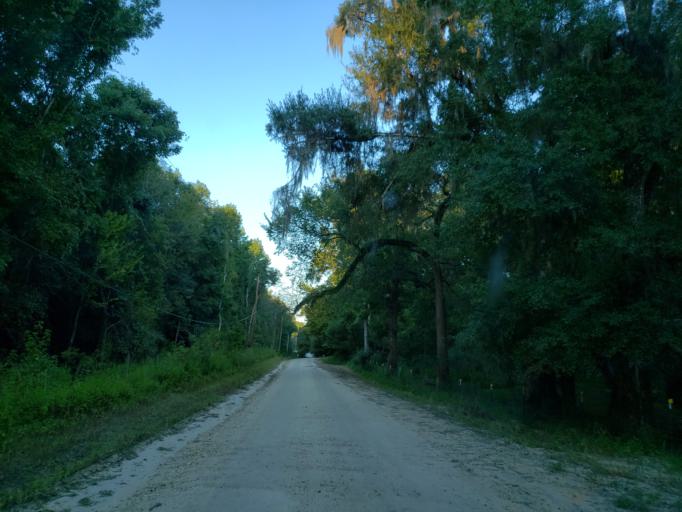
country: US
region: Florida
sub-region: Marion County
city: Citra
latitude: 29.4842
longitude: -82.2482
